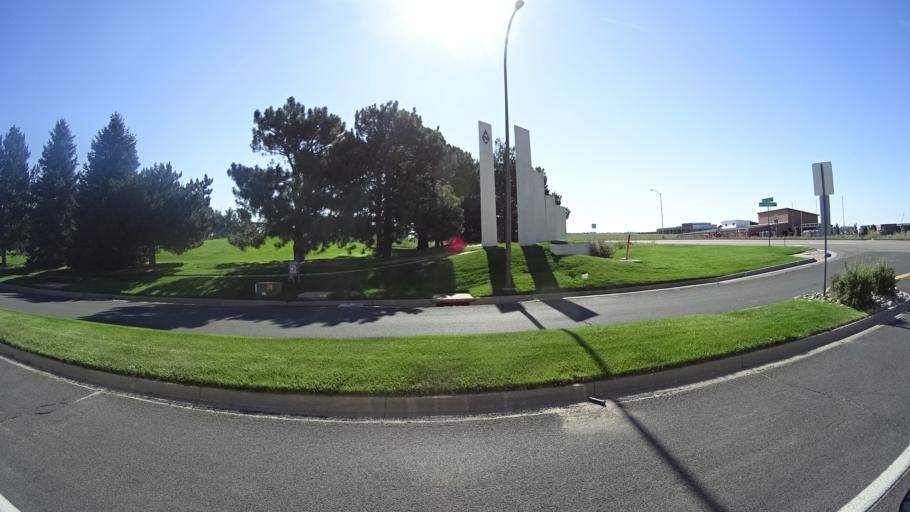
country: US
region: Colorado
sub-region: El Paso County
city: Gleneagle
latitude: 38.9950
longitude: -104.7934
